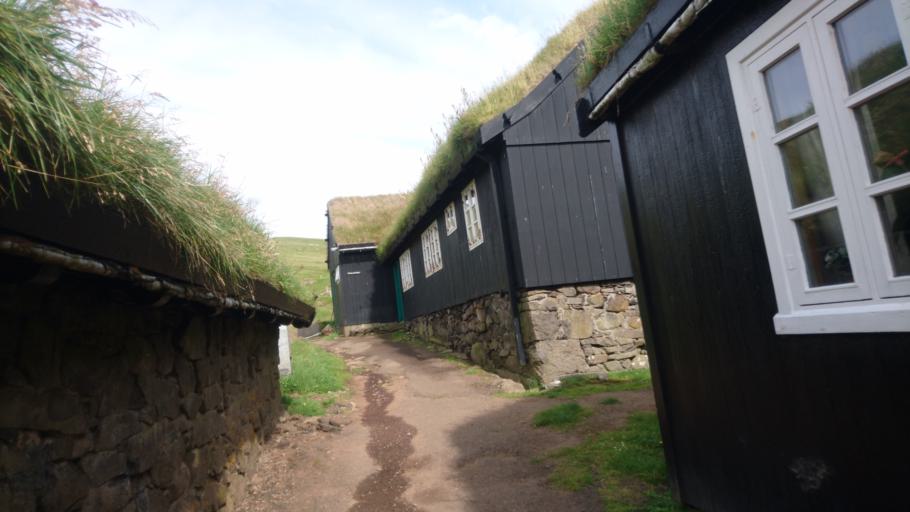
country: FO
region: Vagar
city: Sorvagur
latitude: 62.1043
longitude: -7.6434
